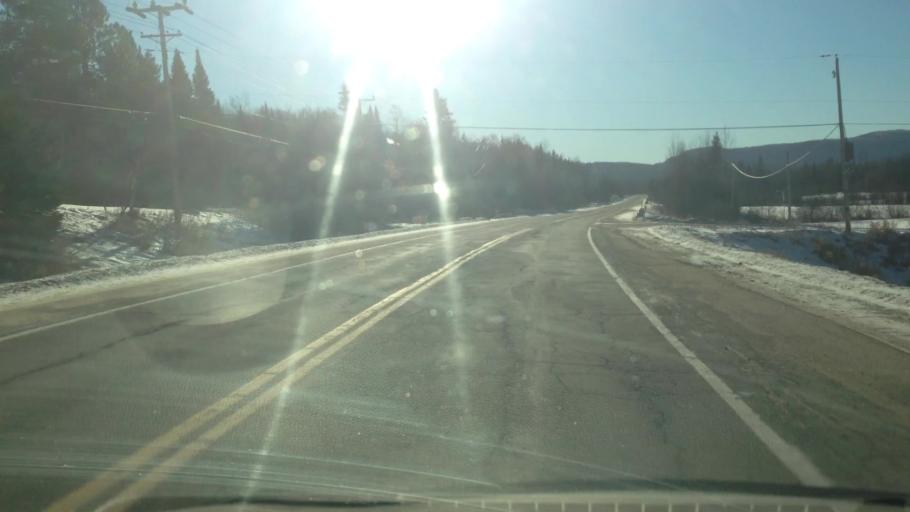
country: CA
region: Quebec
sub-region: Laurentides
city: Mont-Tremblant
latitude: 46.0798
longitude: -74.6142
